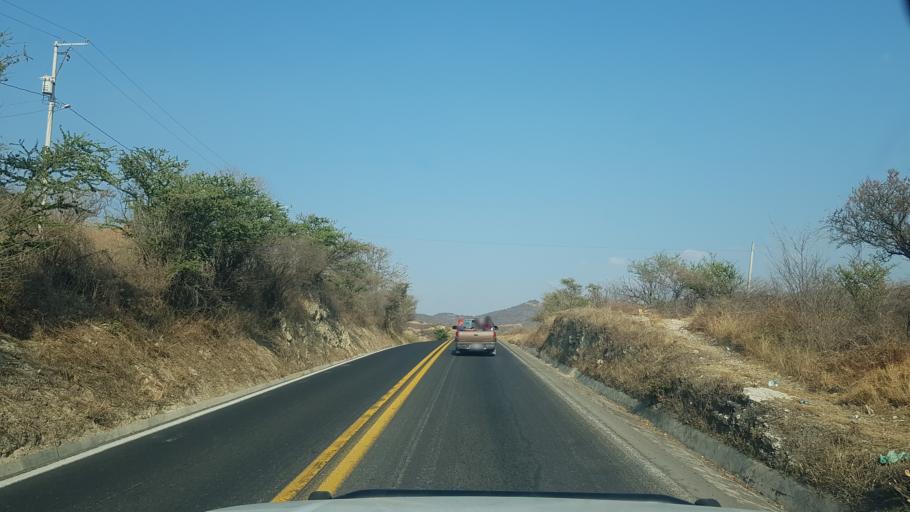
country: MX
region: Puebla
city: Calmeca
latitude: 18.6431
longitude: -98.6265
